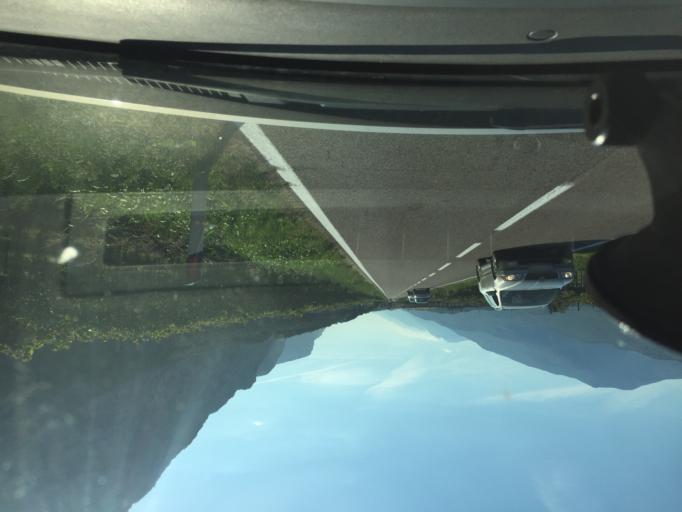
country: IT
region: Trentino-Alto Adige
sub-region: Provincia di Trento
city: Pietramurata
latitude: 46.0395
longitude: 10.9501
